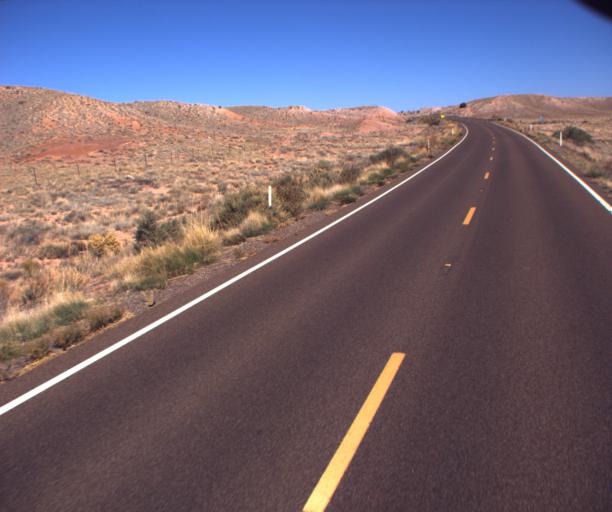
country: US
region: Arizona
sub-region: Navajo County
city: Joseph City
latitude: 35.1729
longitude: -110.4446
